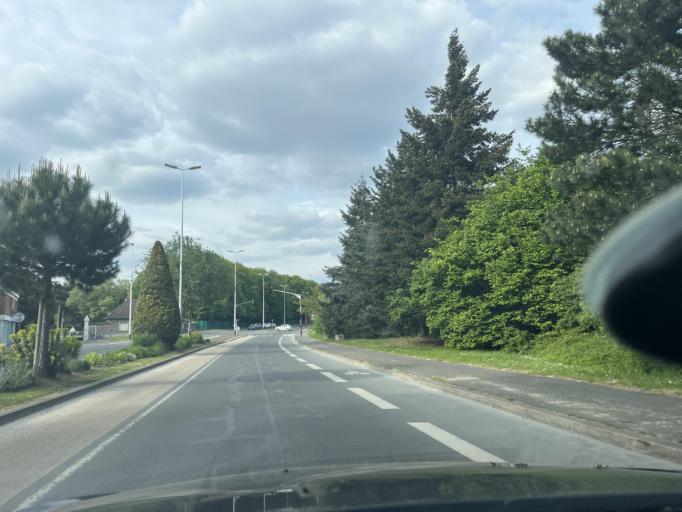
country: FR
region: Ile-de-France
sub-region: Departement de Seine-Saint-Denis
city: La Courneuve
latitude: 48.9365
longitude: 2.4037
